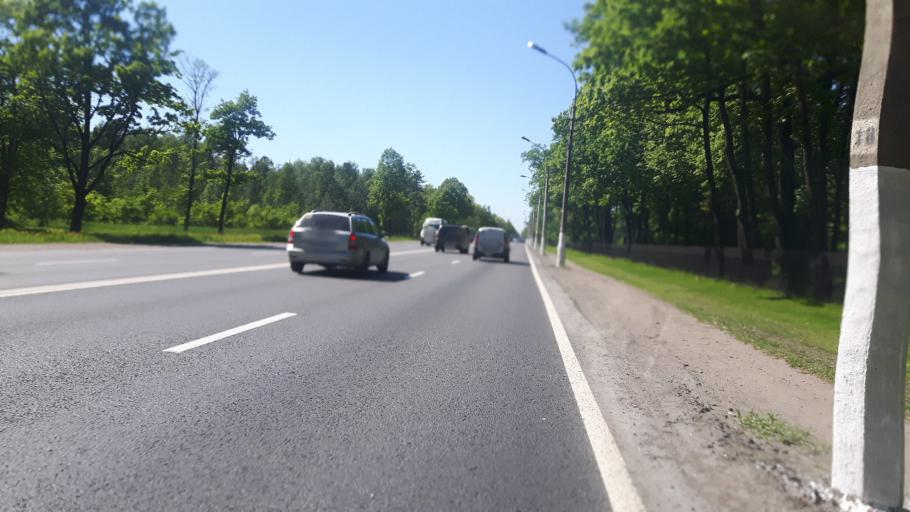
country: RU
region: St.-Petersburg
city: Peterhof
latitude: 59.8758
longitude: 29.9392
